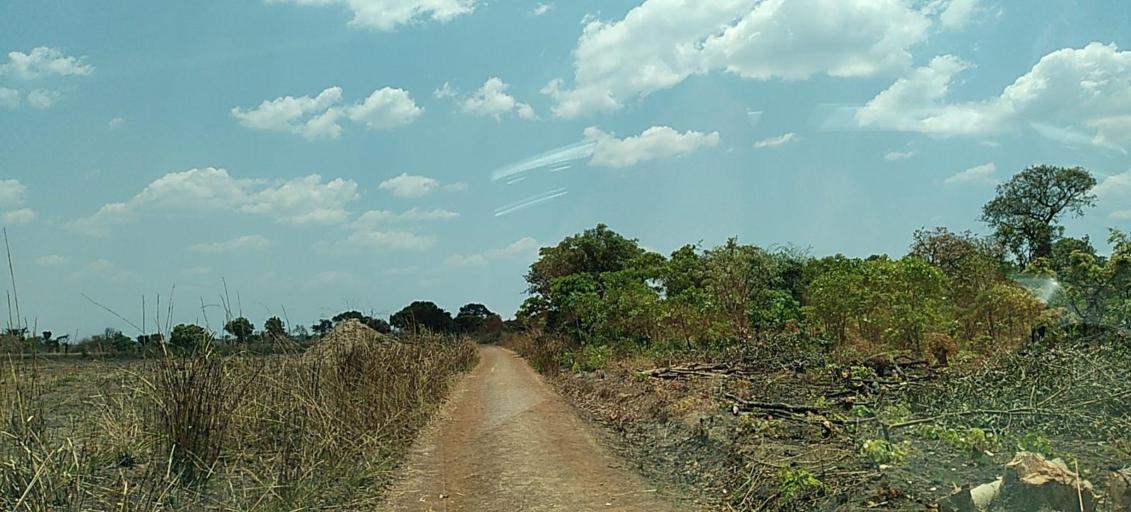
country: ZM
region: Copperbelt
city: Chililabombwe
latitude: -12.4906
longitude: 27.6659
